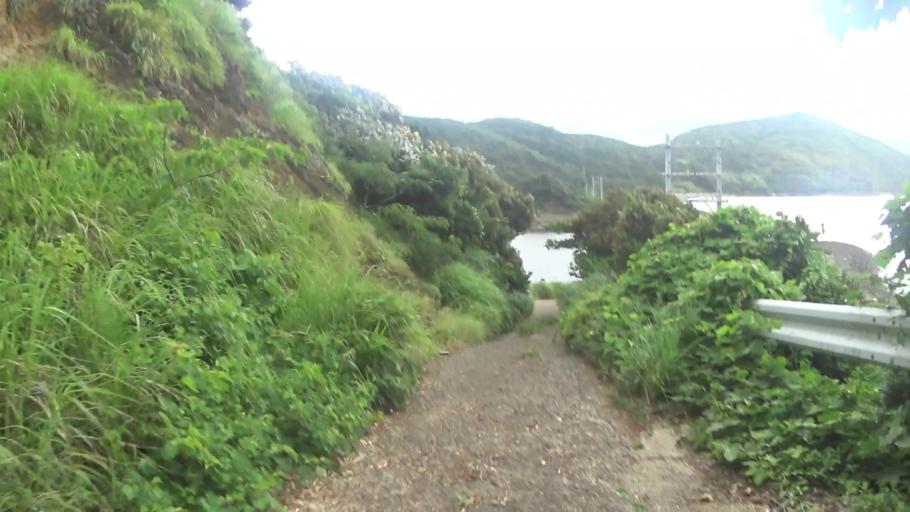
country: JP
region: Nagasaki
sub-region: Hirado Shi
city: Hirado
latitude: 33.1822
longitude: 129.3502
